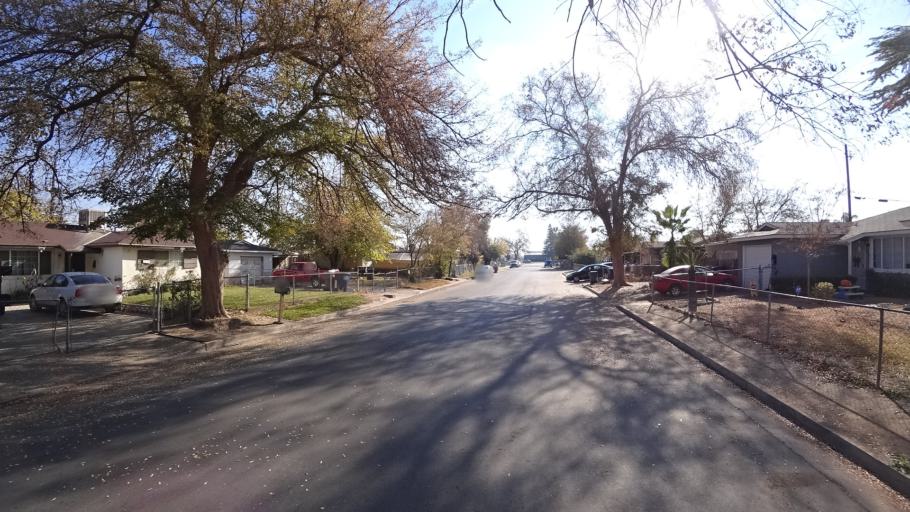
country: US
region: California
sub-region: Kern County
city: Bakersfield
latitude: 35.3264
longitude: -119.0124
